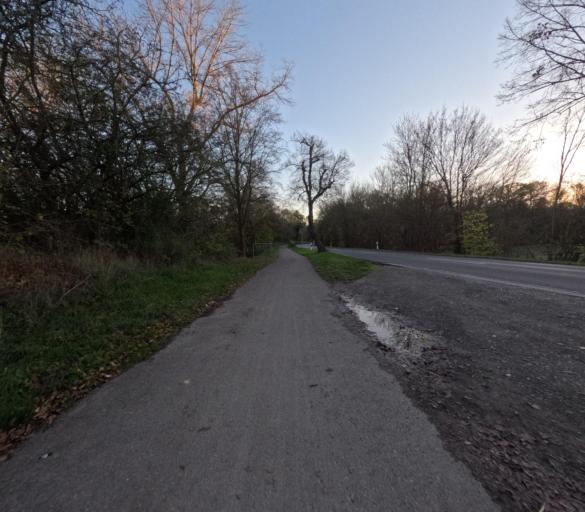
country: DE
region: Saxony
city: Schkeuditz
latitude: 51.3834
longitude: 12.2239
